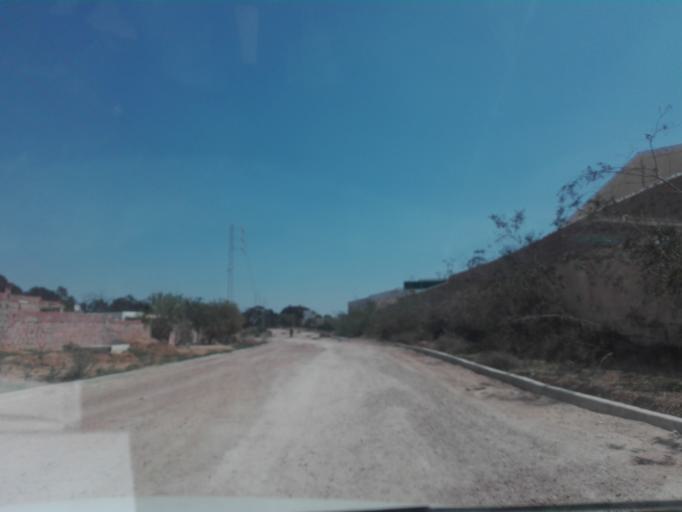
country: TN
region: Safaqis
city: Sfax
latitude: 34.7291
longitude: 10.5201
